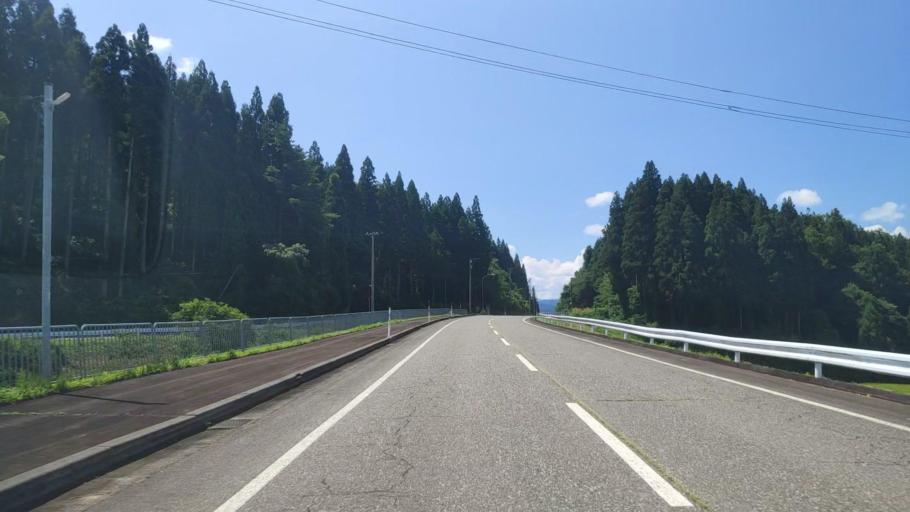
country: JP
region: Fukui
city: Katsuyama
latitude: 36.1008
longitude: 136.4919
